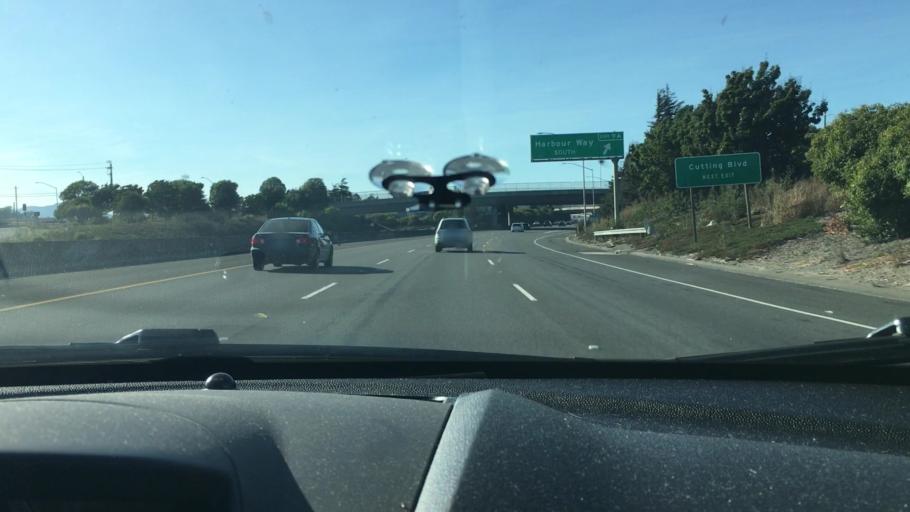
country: US
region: California
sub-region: Contra Costa County
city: Richmond
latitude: 37.9226
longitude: -122.3578
